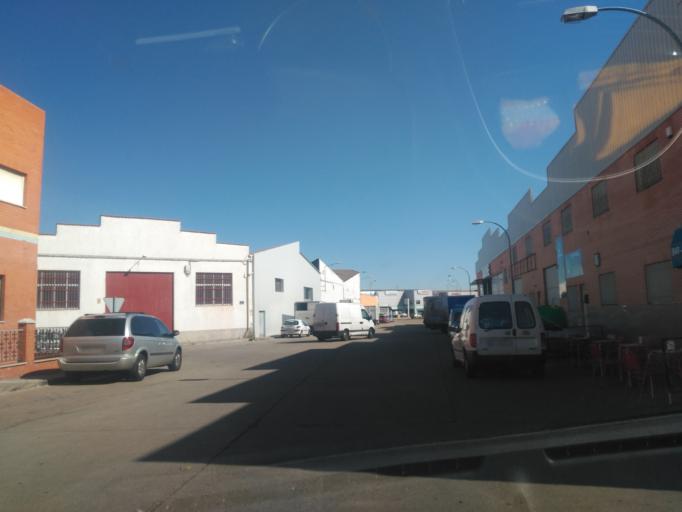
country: ES
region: Castille and Leon
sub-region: Provincia de Salamanca
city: Villares de la Reina
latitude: 40.9939
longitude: -5.6353
